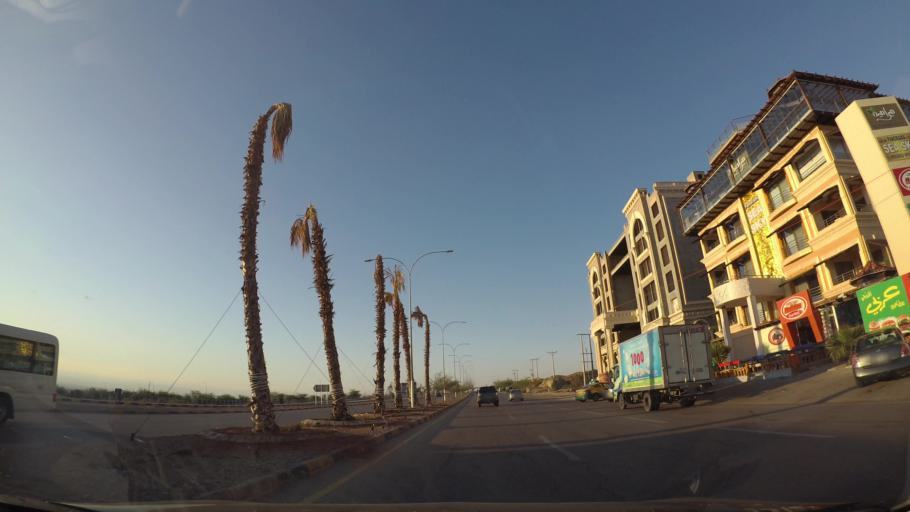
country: PS
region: West Bank
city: Jericho
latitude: 31.7518
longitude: 35.5946
